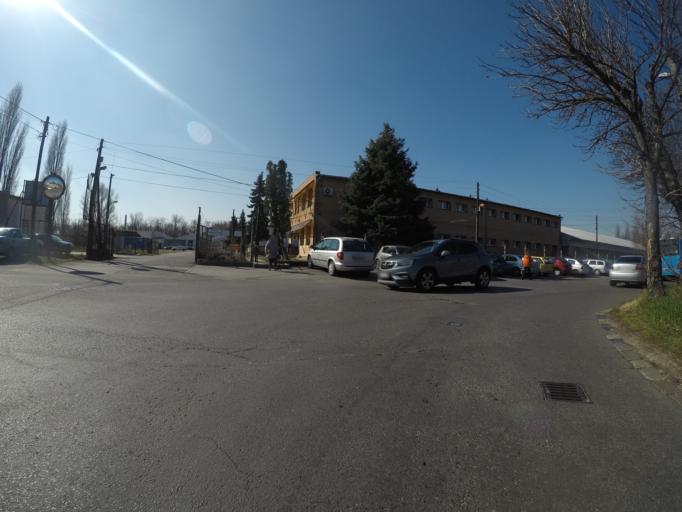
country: HU
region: Budapest
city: Budapest XIX. keruelet
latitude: 47.4349
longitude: 19.1544
